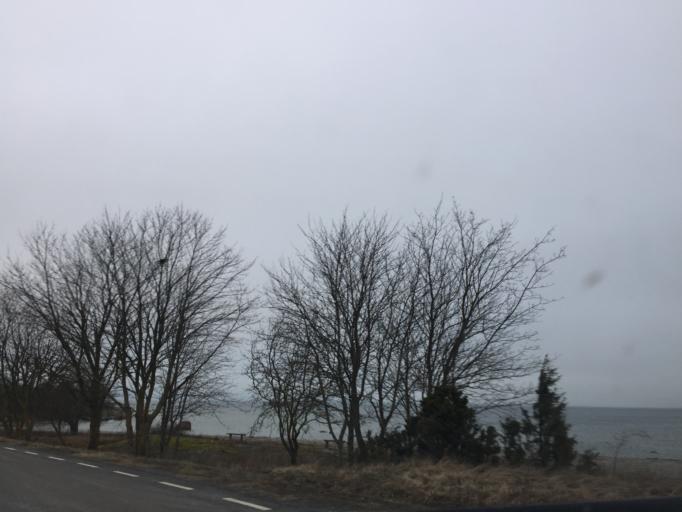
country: EE
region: Saare
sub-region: Kuressaare linn
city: Kuressaare
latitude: 58.5646
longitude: 22.3125
